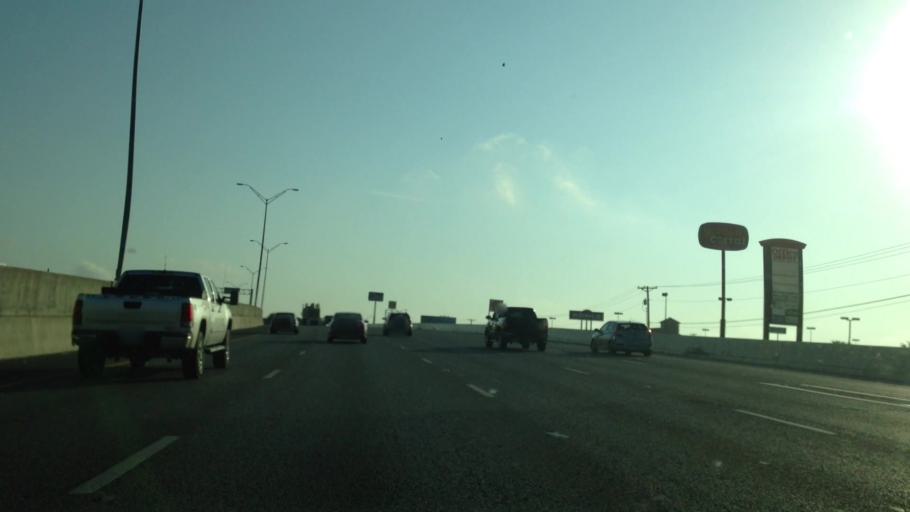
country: US
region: Texas
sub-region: Comal County
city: New Braunfels
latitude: 29.6960
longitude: -98.0961
